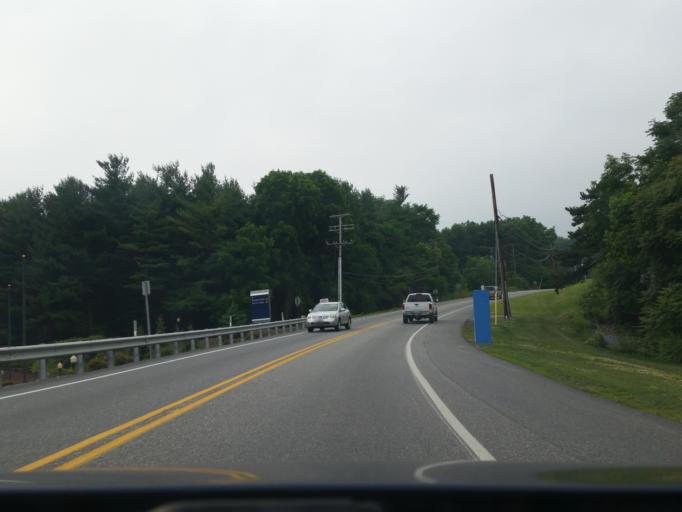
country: US
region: Pennsylvania
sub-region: Lebanon County
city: Annville
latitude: 40.3352
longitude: -76.5191
